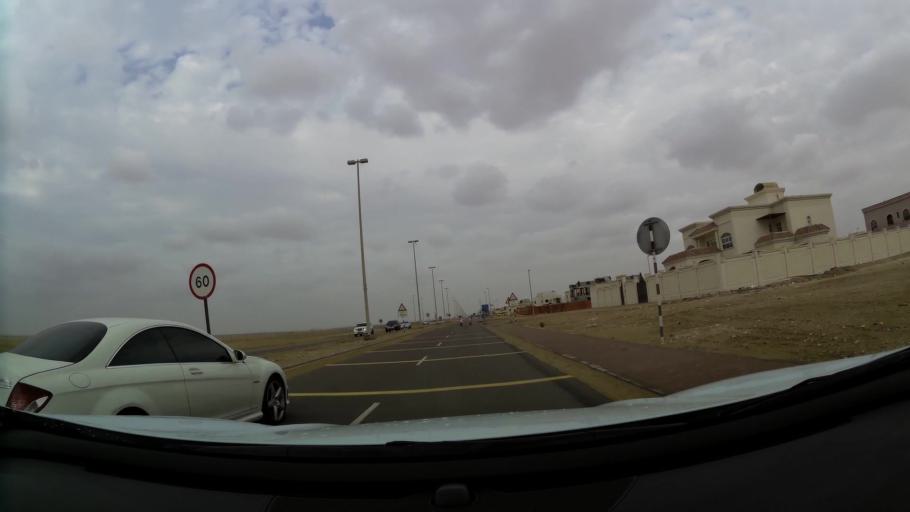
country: AE
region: Abu Dhabi
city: Abu Dhabi
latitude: 24.3616
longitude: 54.6171
